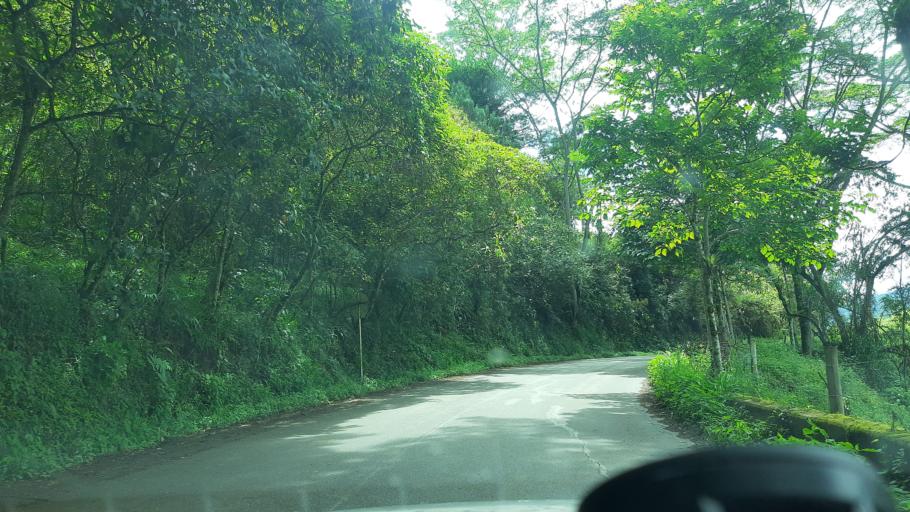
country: CO
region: Boyaca
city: Garagoa
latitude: 5.1039
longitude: -73.3676
